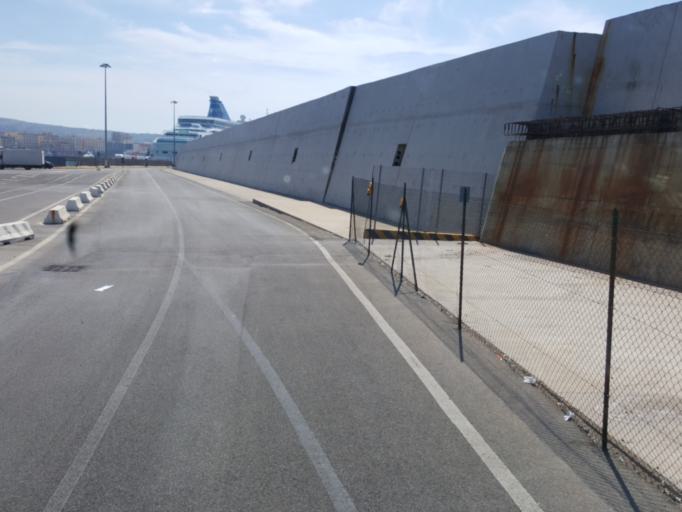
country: IT
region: Latium
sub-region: Citta metropolitana di Roma Capitale
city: Civitavecchia
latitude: 42.0934
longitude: 11.7797
